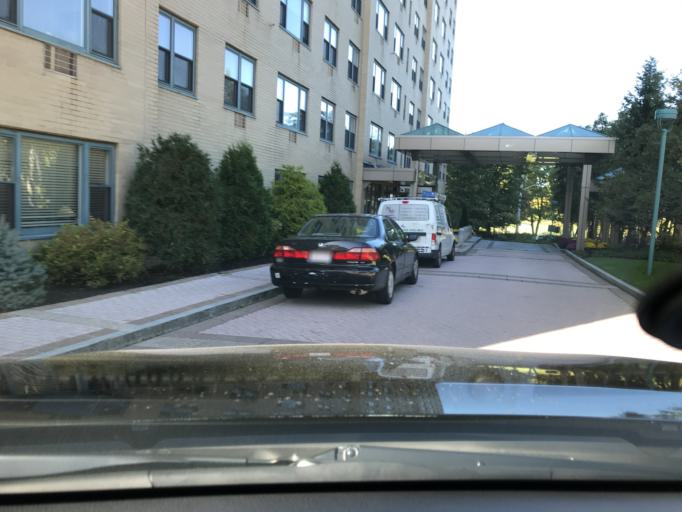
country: US
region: Massachusetts
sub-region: Middlesex County
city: Belmont
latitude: 42.3807
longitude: -71.1542
